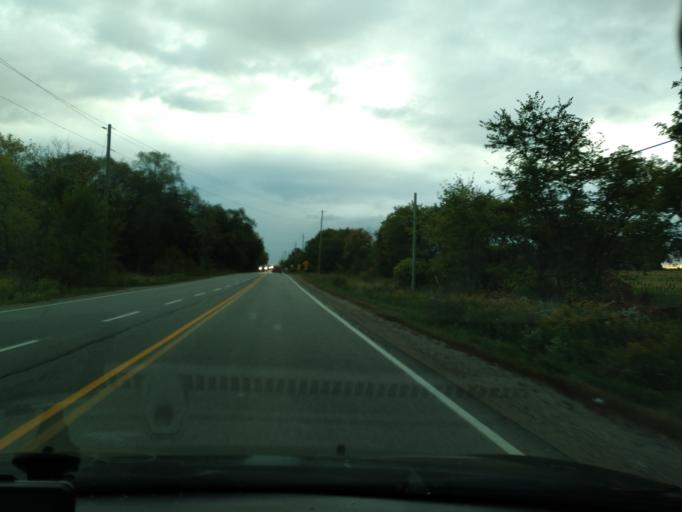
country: CA
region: Ontario
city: Innisfil
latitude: 44.2964
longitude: -79.5717
